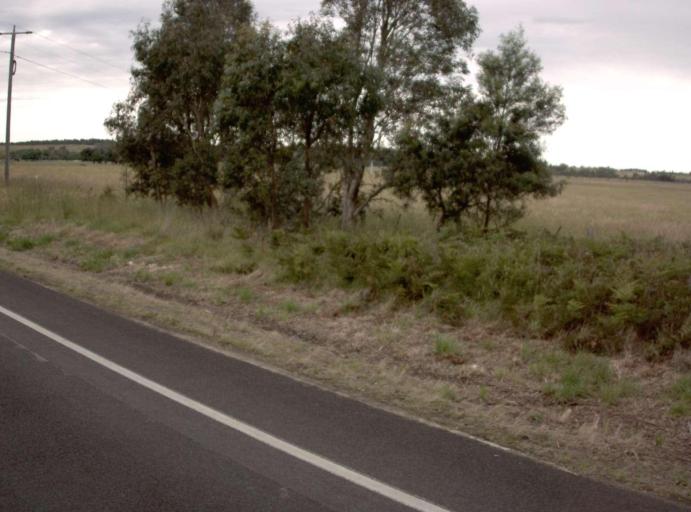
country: AU
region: Victoria
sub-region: Wellington
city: Sale
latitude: -38.3021
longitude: 147.0321
